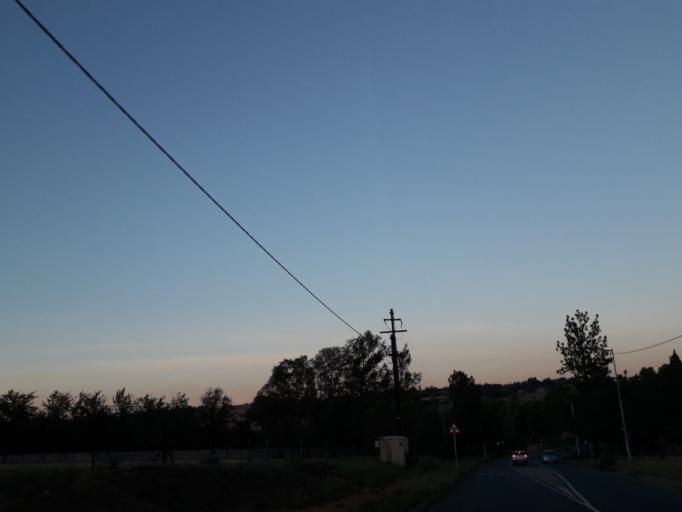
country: ZA
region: Gauteng
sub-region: West Rand District Municipality
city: Muldersdriseloop
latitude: -26.0868
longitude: 27.9003
